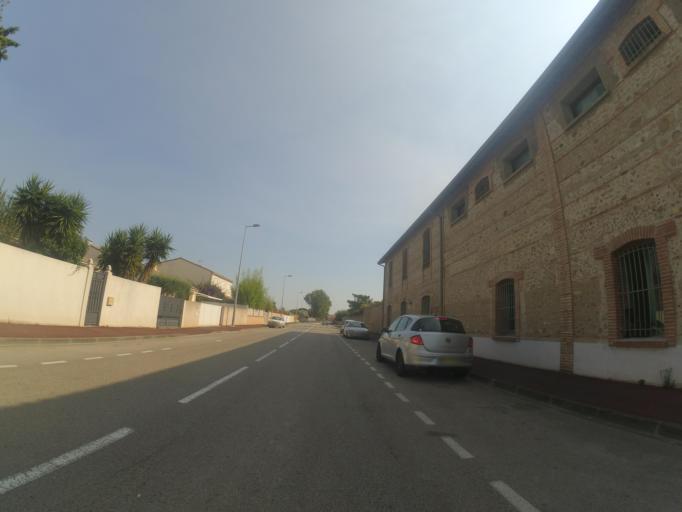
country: FR
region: Languedoc-Roussillon
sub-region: Departement des Pyrenees-Orientales
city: Toulouges
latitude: 42.6657
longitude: 2.8371
